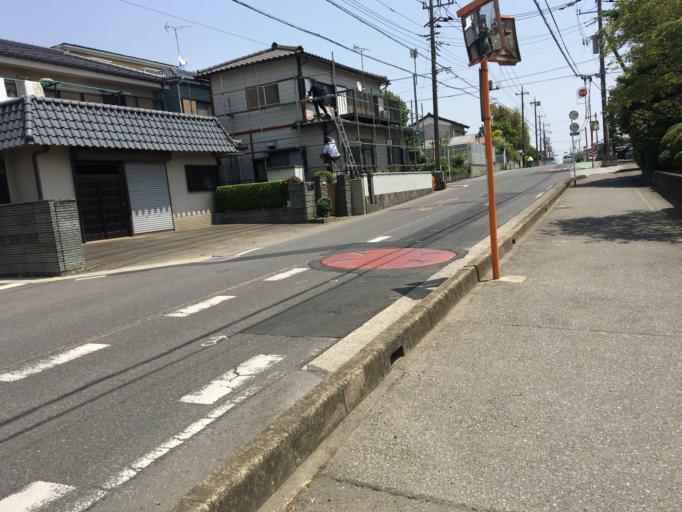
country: JP
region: Saitama
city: Kasukabe
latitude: 35.9745
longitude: 139.7172
